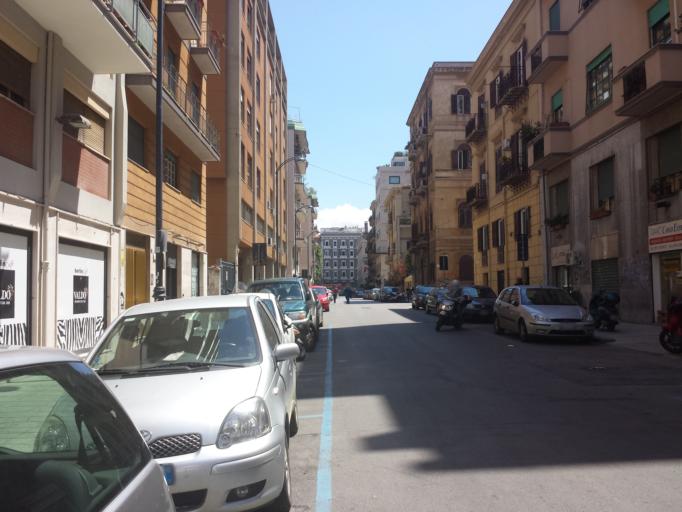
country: IT
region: Sicily
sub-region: Palermo
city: Palermo
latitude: 38.1268
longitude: 13.3563
